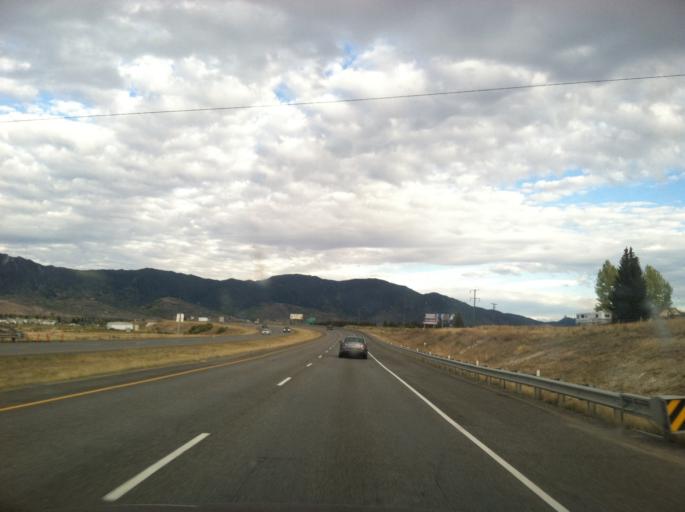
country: US
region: Montana
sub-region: Silver Bow County
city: Butte
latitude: 45.9935
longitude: -112.5575
